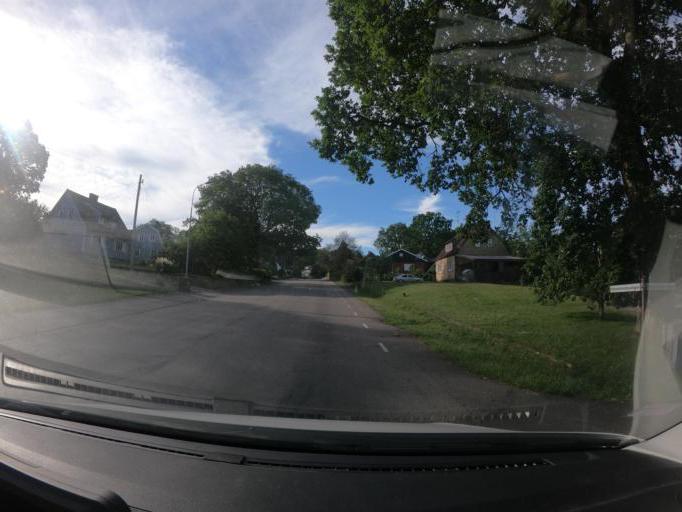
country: SE
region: Skane
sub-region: Orkelljunga Kommun
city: OErkelljunga
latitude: 56.2742
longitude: 13.2872
